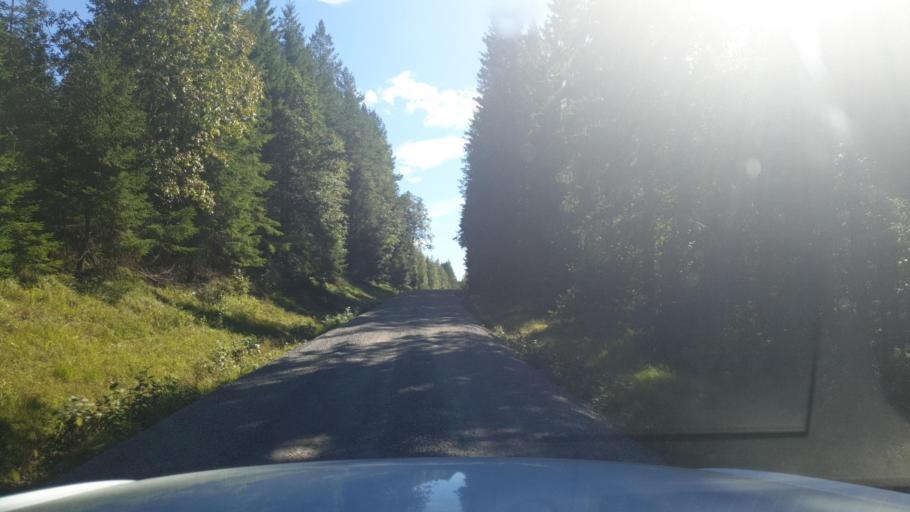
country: SE
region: Vaermland
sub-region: Eda Kommun
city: Charlottenberg
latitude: 60.0549
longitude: 12.6277
